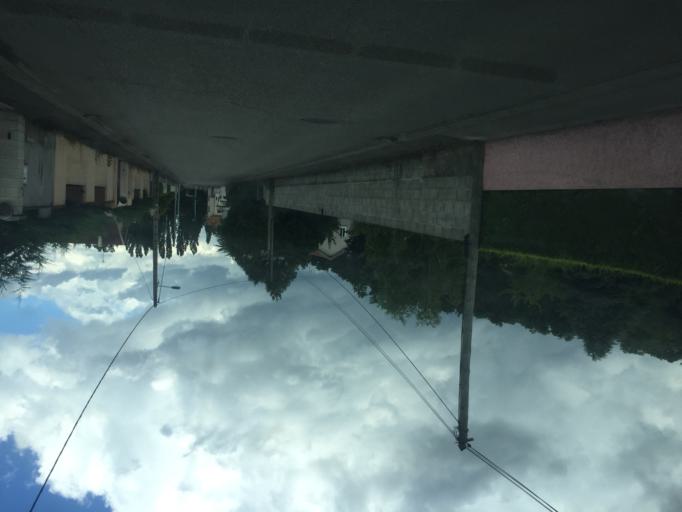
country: FR
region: Rhone-Alpes
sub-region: Departement de l'Isere
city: Pont-de-Cheruy
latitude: 45.7622
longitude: 5.1769
